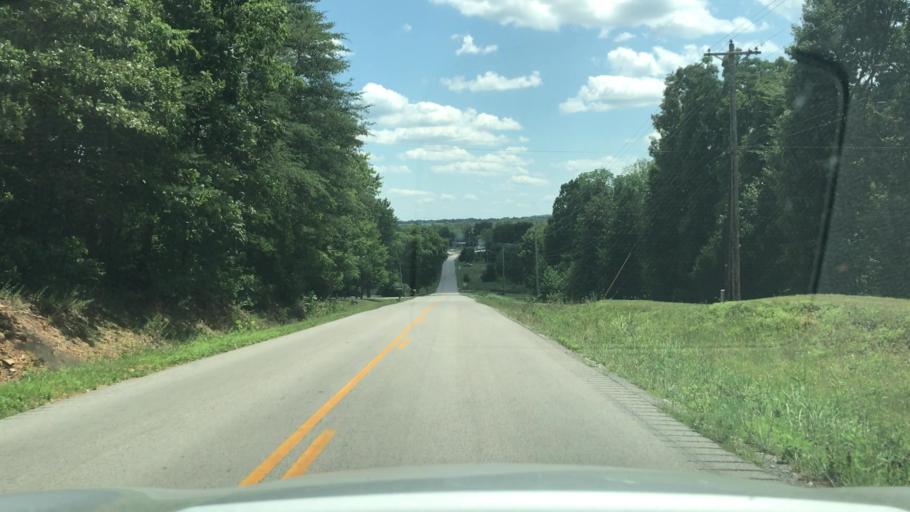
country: US
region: Kentucky
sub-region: Christian County
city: Hopkinsville
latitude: 36.9902
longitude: -87.3614
